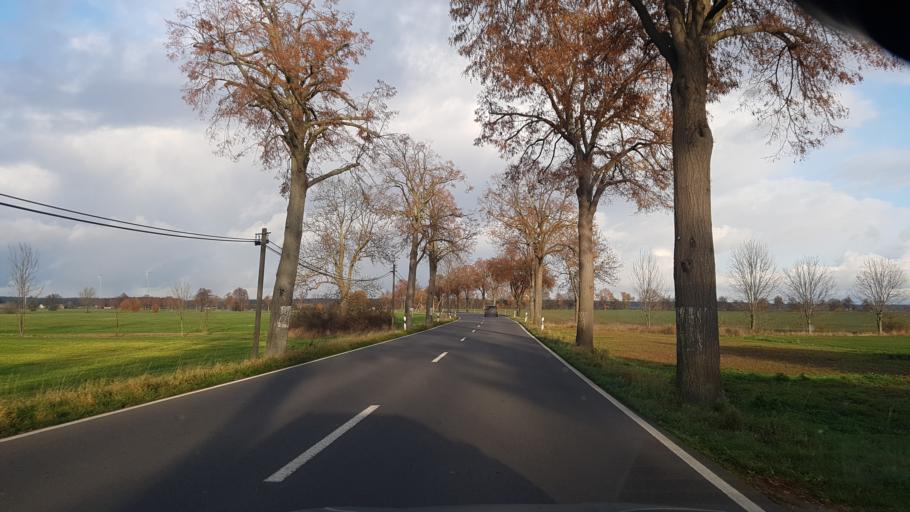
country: DE
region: Brandenburg
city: Sonnewalde
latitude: 51.7014
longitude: 13.6605
